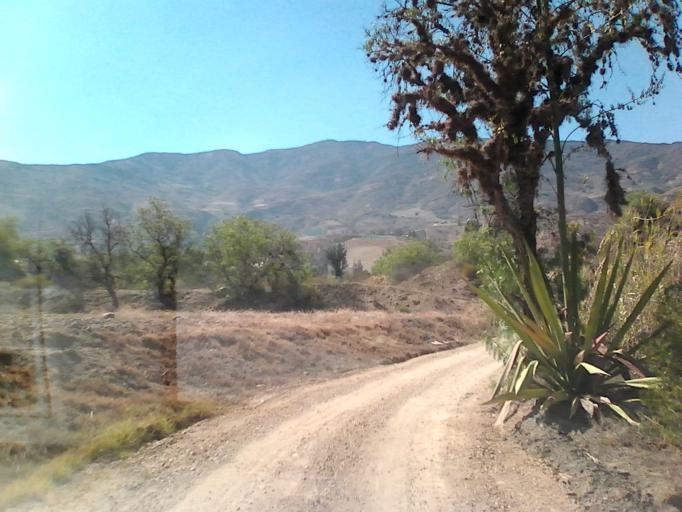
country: CO
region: Boyaca
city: Sachica
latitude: 5.5681
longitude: -73.5493
